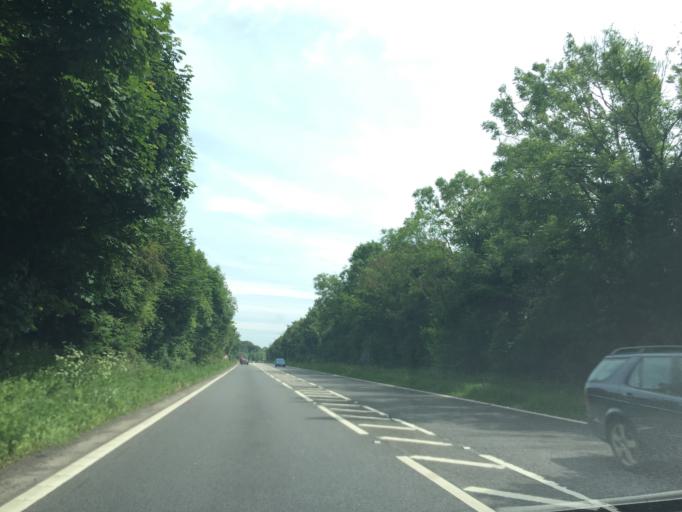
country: GB
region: England
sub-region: Kent
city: Dover
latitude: 51.1576
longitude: 1.2787
